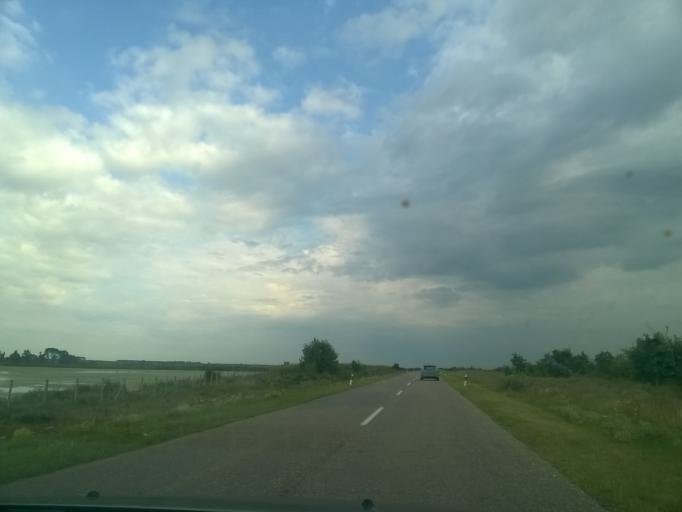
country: RS
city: Uzdin
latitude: 45.2199
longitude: 20.6302
